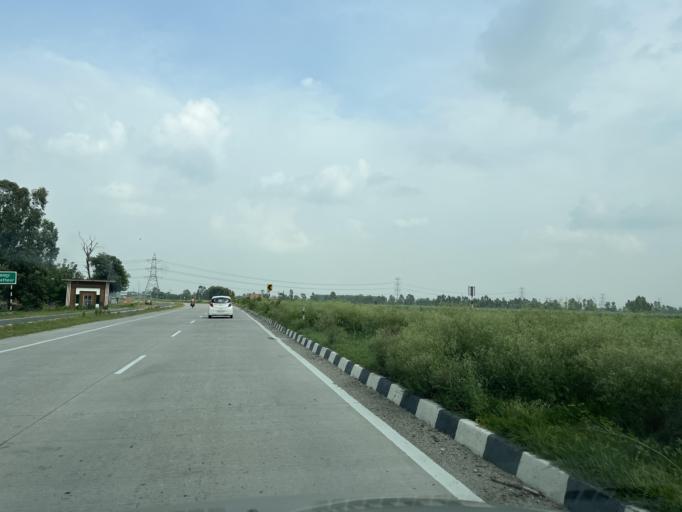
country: IN
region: Uttarakhand
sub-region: Udham Singh Nagar
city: Bazpur
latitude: 29.1497
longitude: 79.0773
